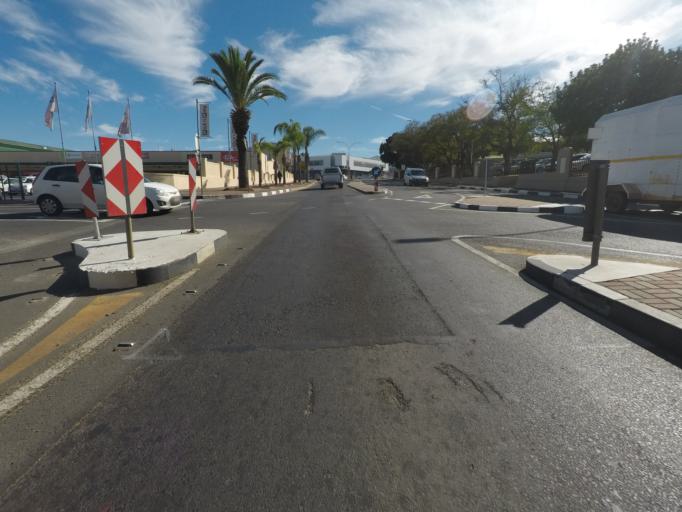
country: ZA
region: Western Cape
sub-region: West Coast District Municipality
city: Malmesbury
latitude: -33.4634
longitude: 18.7293
